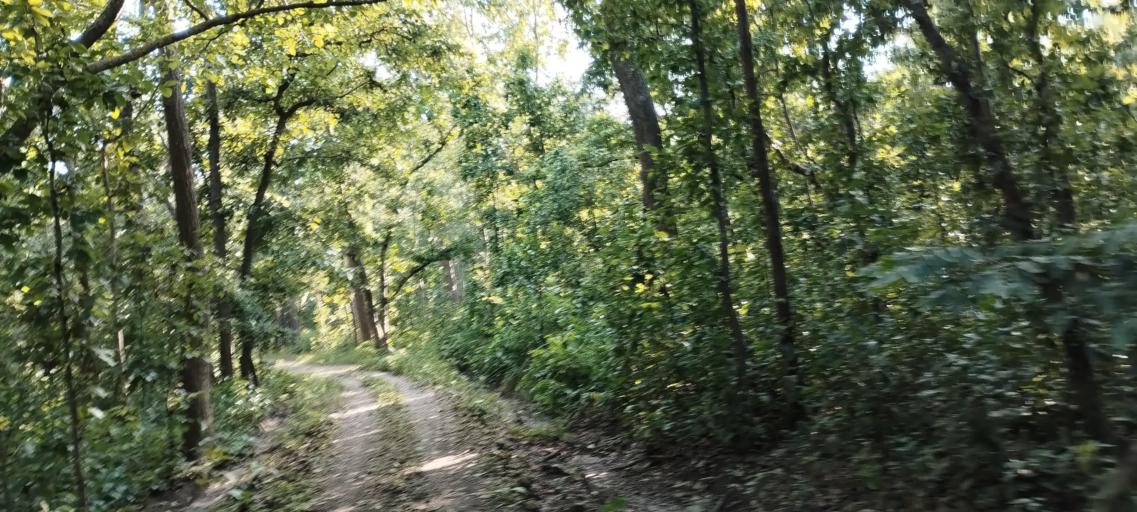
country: NP
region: Far Western
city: Tikapur
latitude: 28.5062
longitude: 81.2663
